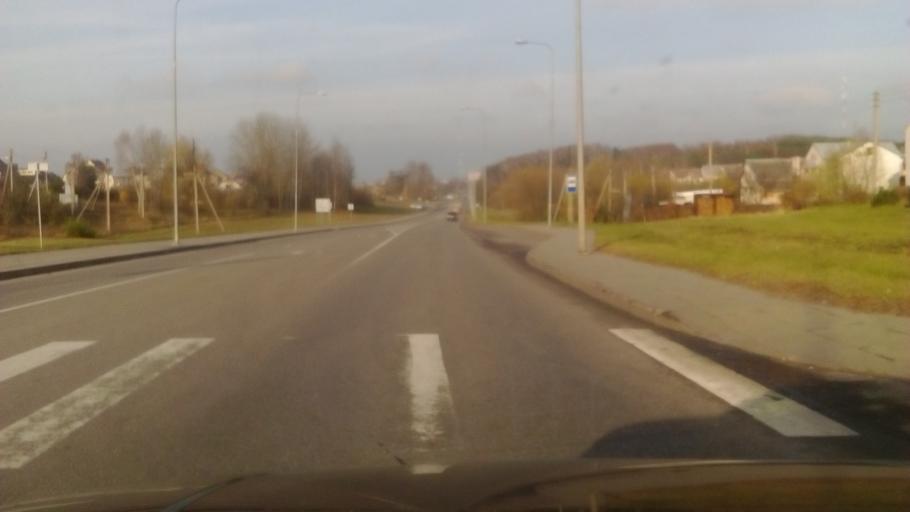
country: LT
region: Alytaus apskritis
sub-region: Alytus
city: Alytus
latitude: 54.3969
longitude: 23.9997
